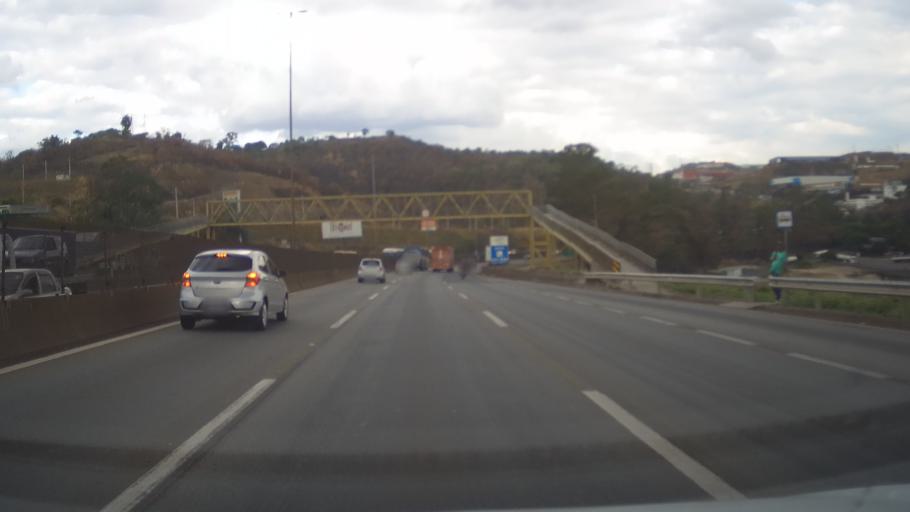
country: BR
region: Minas Gerais
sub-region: Contagem
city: Contagem
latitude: -19.9558
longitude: -44.0981
